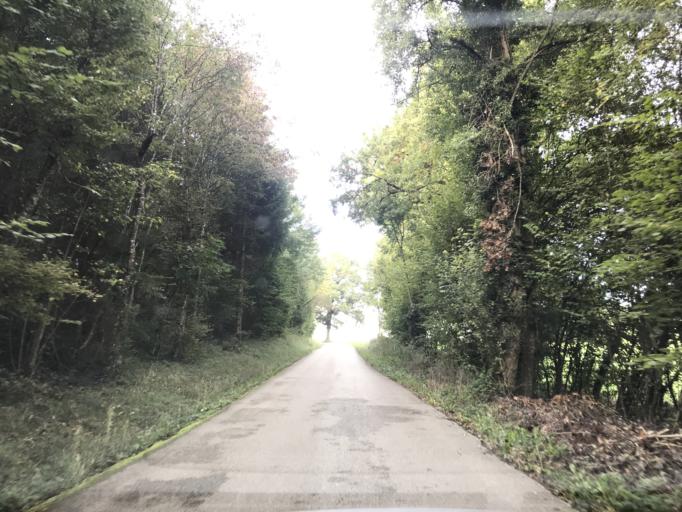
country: FR
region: Rhone-Alpes
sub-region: Departement de la Savoie
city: Yenne
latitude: 45.6889
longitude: 5.7965
